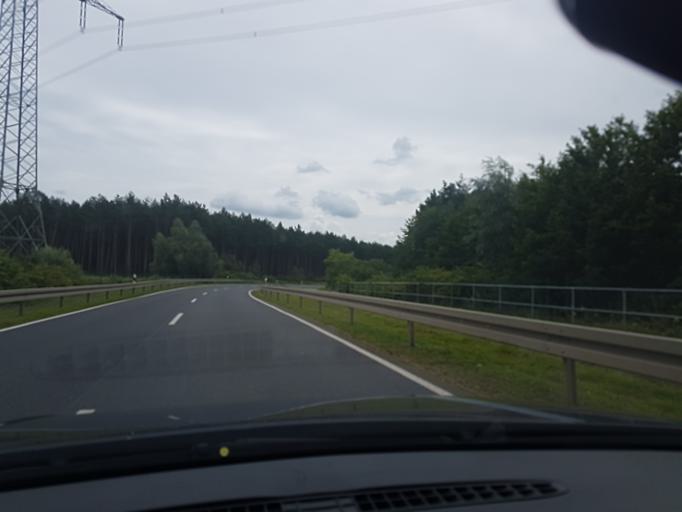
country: DE
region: Brandenburg
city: Velten
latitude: 52.6765
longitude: 13.2008
